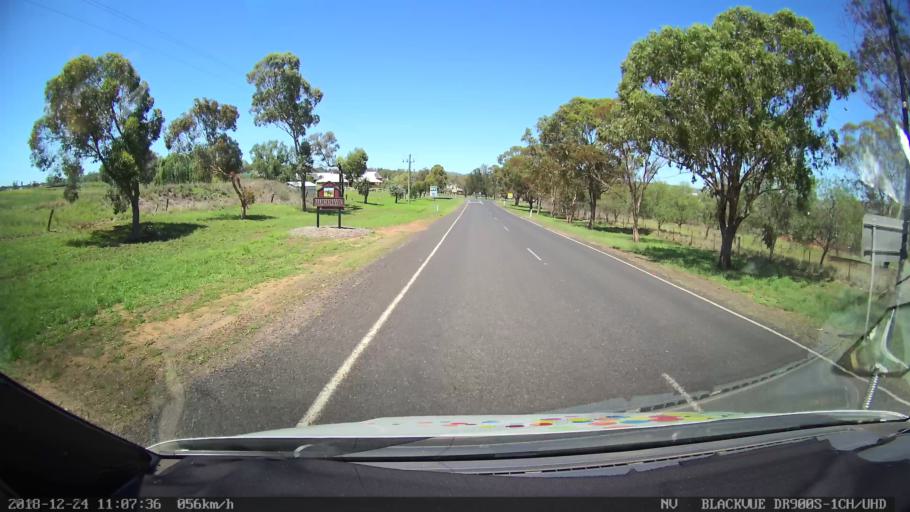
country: AU
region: New South Wales
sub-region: Upper Hunter Shire
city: Merriwa
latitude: -32.1341
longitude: 150.3589
